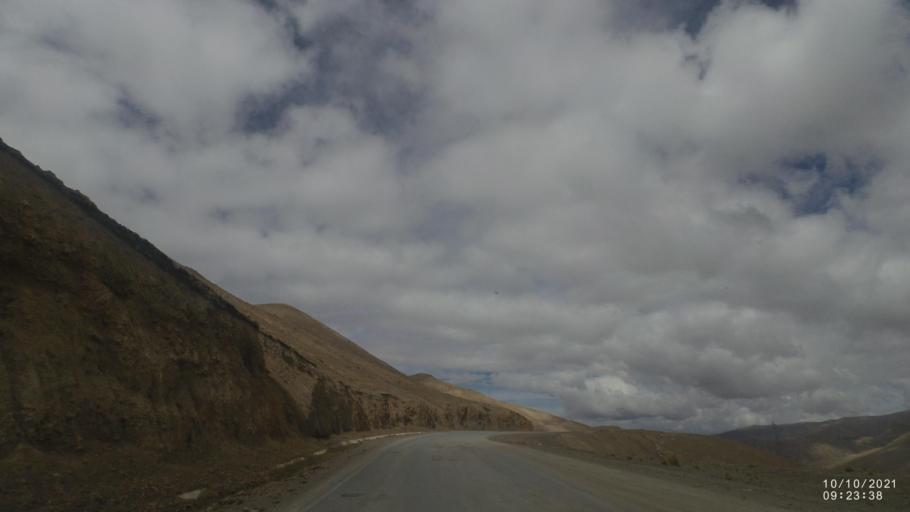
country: BO
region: La Paz
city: Quime
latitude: -17.0862
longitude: -67.3044
